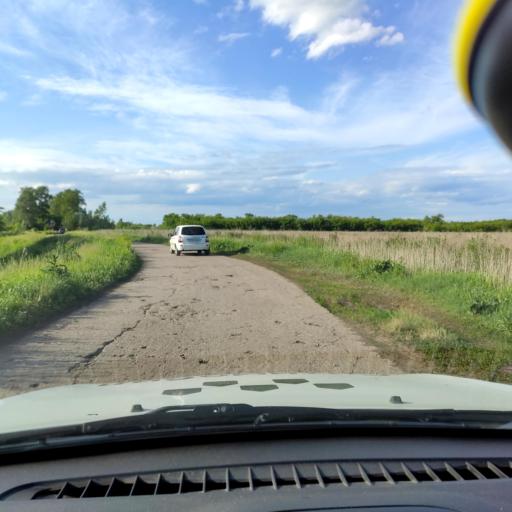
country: RU
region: Samara
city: Tol'yatti
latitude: 53.5956
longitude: 49.4572
